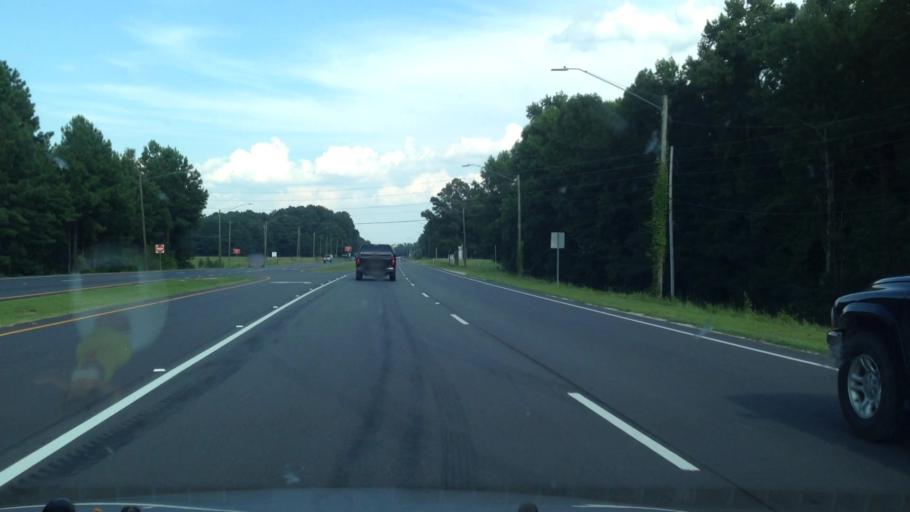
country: US
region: North Carolina
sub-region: Harnett County
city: Lillington
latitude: 35.4101
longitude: -78.7806
